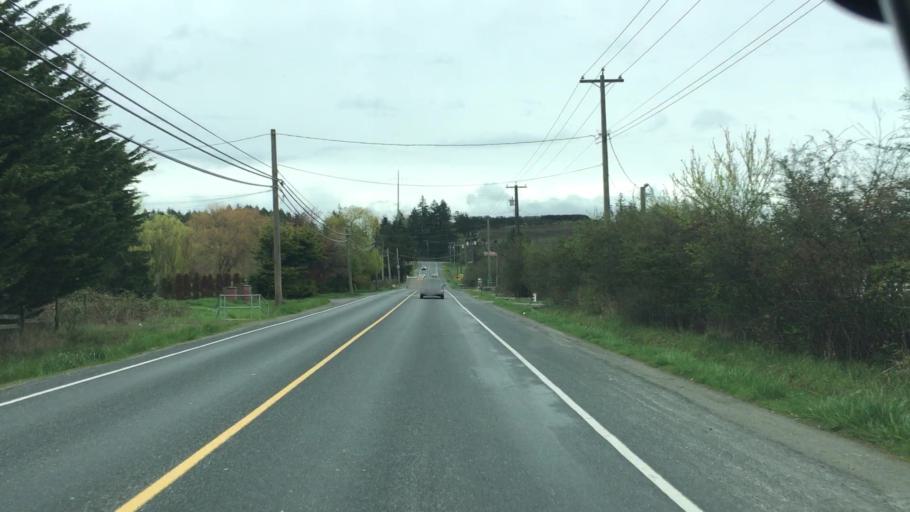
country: CA
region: British Columbia
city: North Saanich
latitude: 48.5651
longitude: -123.4351
